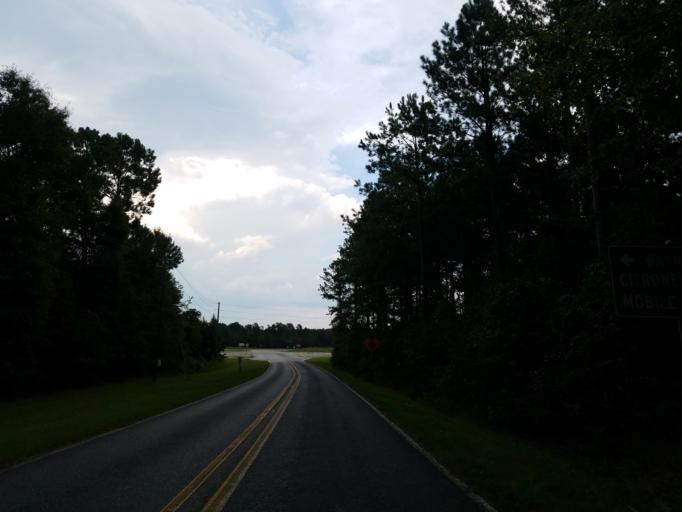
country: US
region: Mississippi
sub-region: Wayne County
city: Belmont
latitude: 31.4465
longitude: -88.4617
